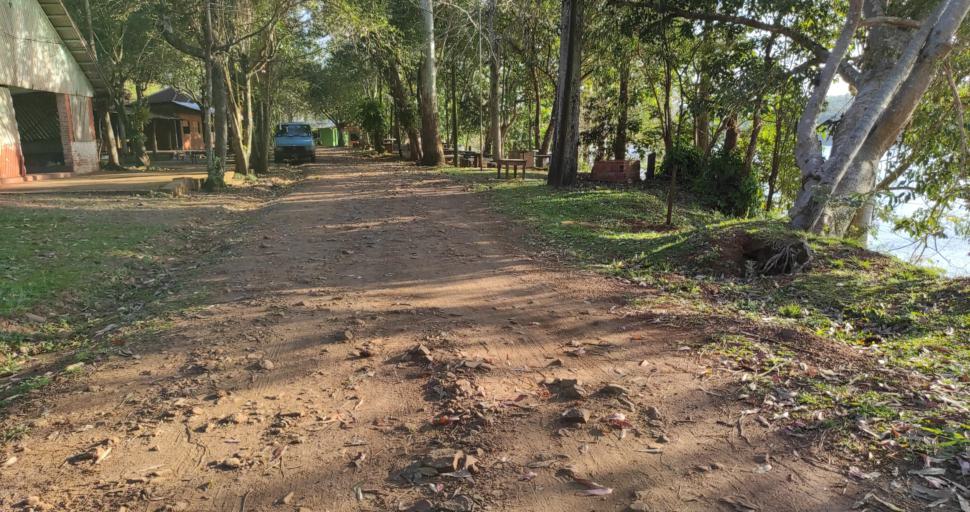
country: AR
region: Misiones
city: Capiovi
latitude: -26.8626
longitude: -55.1352
